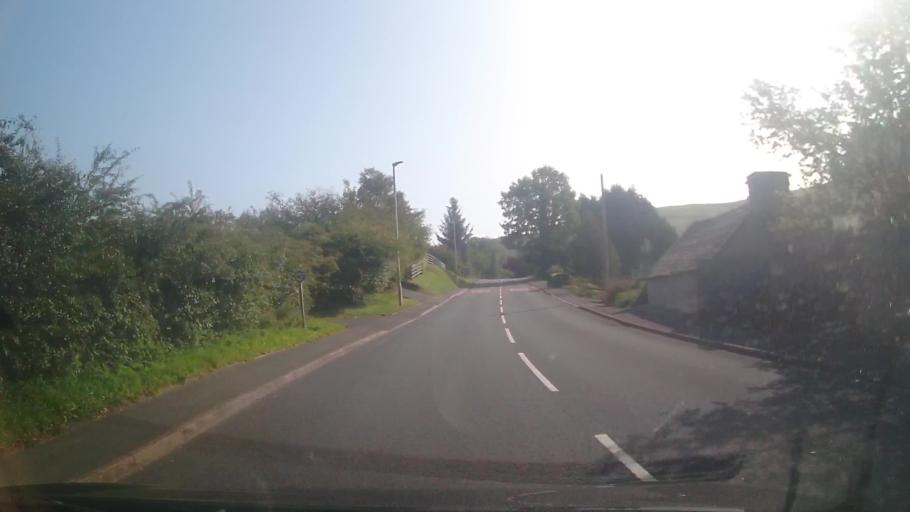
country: GB
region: Wales
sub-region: Sir Powys
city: Rhayader
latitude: 52.2980
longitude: -3.5050
